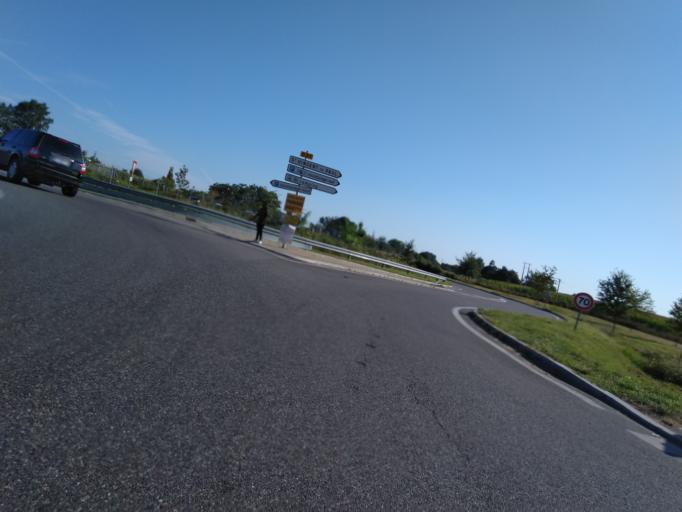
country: FR
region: Aquitaine
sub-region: Departement des Landes
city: Saint-Vincent-de-Paul
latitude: 43.7383
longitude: -1.0163
